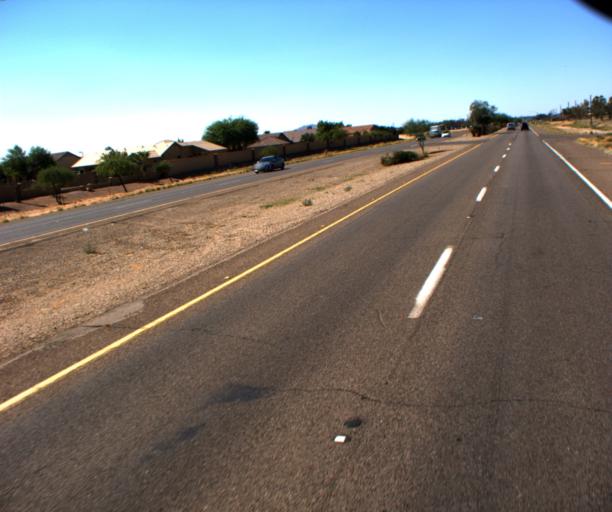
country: US
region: Arizona
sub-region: Pinal County
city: Casa Grande
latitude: 32.9290
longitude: -111.7570
